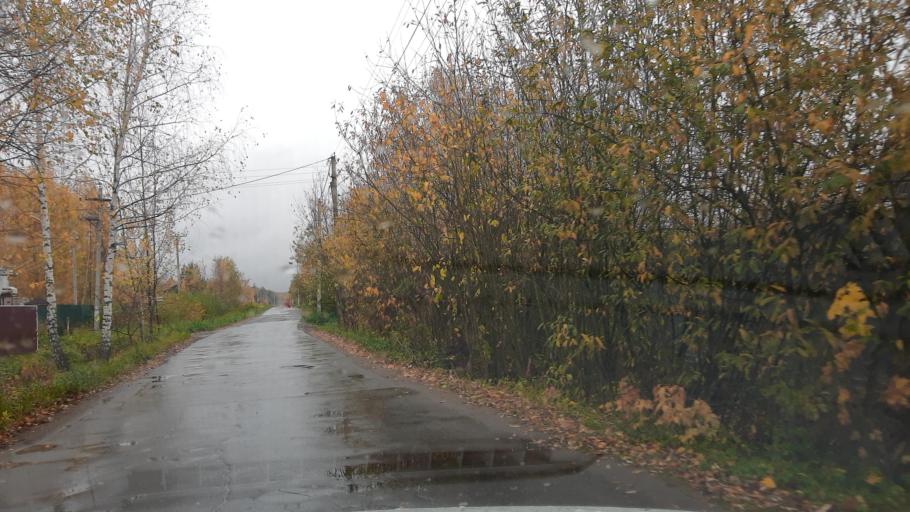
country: RU
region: Moskovskaya
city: Imeni Vorovskogo
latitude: 55.7820
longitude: 38.3633
